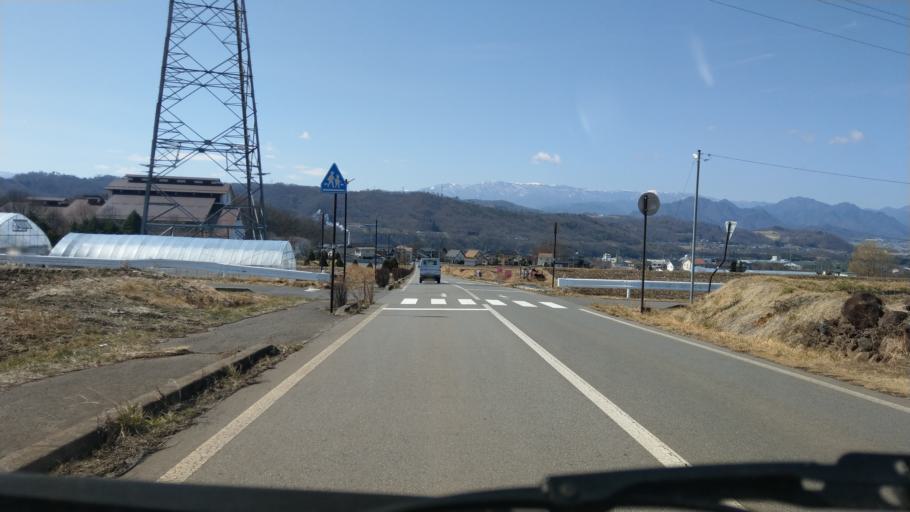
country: JP
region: Nagano
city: Ueda
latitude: 36.3627
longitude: 138.3412
